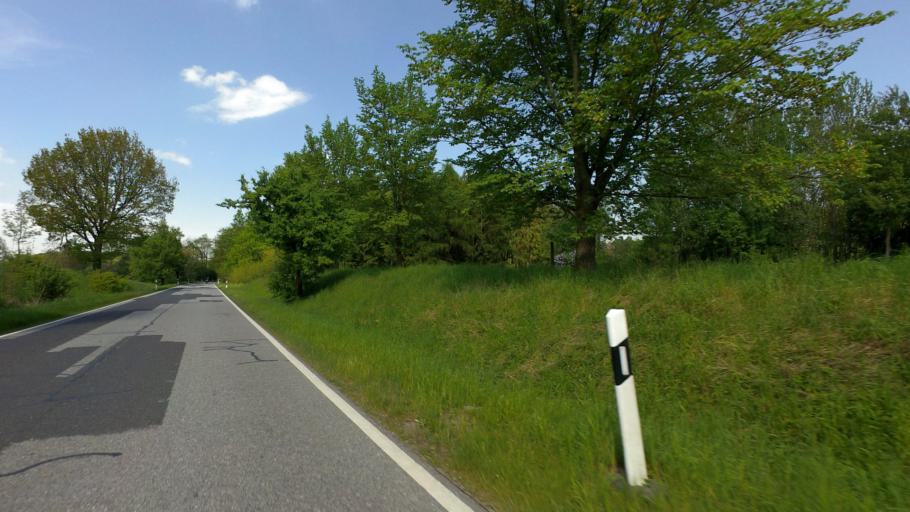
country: DE
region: Mecklenburg-Vorpommern
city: Mollenhagen
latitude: 53.5509
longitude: 12.9222
